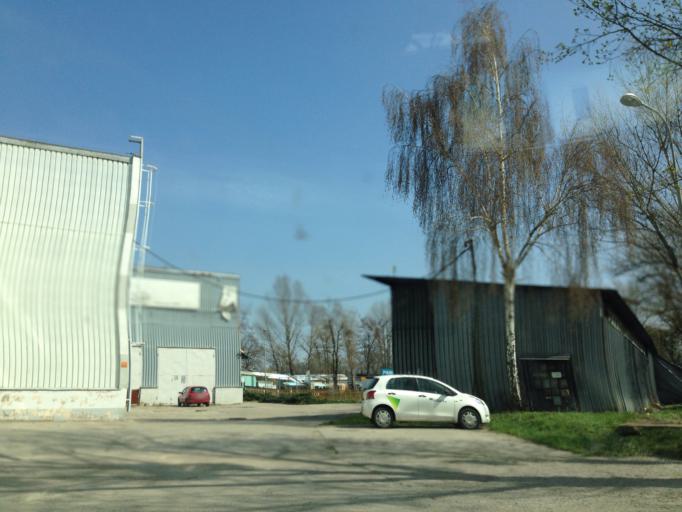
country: PL
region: Lower Silesian Voivodeship
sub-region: Powiat wroclawski
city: Wilczyce
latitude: 51.1012
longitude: 17.1195
